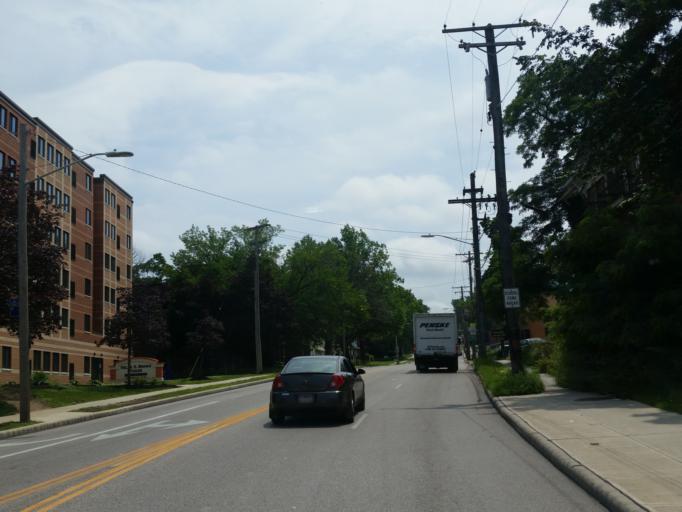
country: US
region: Ohio
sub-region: Cuyahoga County
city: East Cleveland
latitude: 41.5433
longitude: -81.5678
